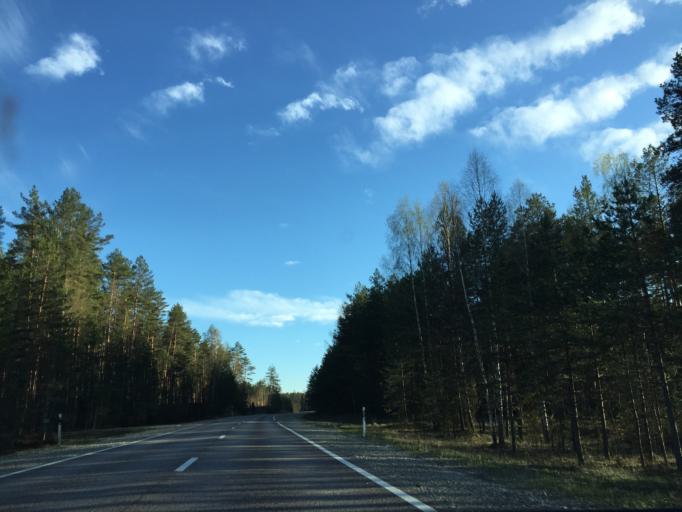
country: LV
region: Strenci
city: Seda
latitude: 57.6605
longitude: 25.8726
